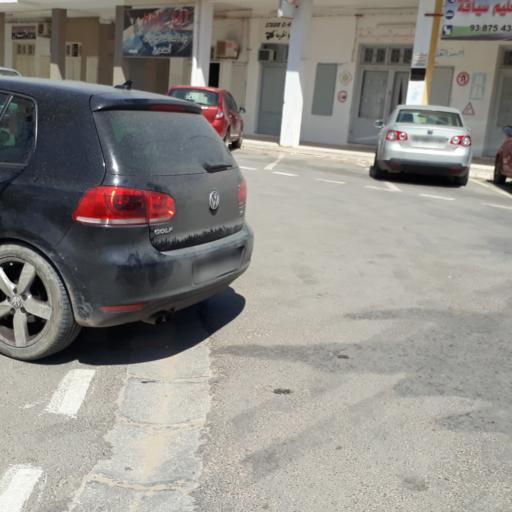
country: TN
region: Safaqis
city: Al Qarmadah
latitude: 34.8037
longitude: 10.7607
